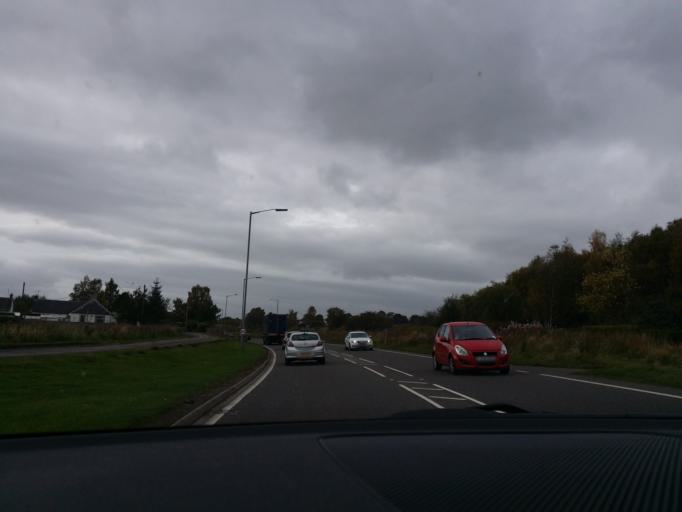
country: GB
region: Scotland
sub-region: Clackmannanshire
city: Clackmannan
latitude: 56.1133
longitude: -3.7490
